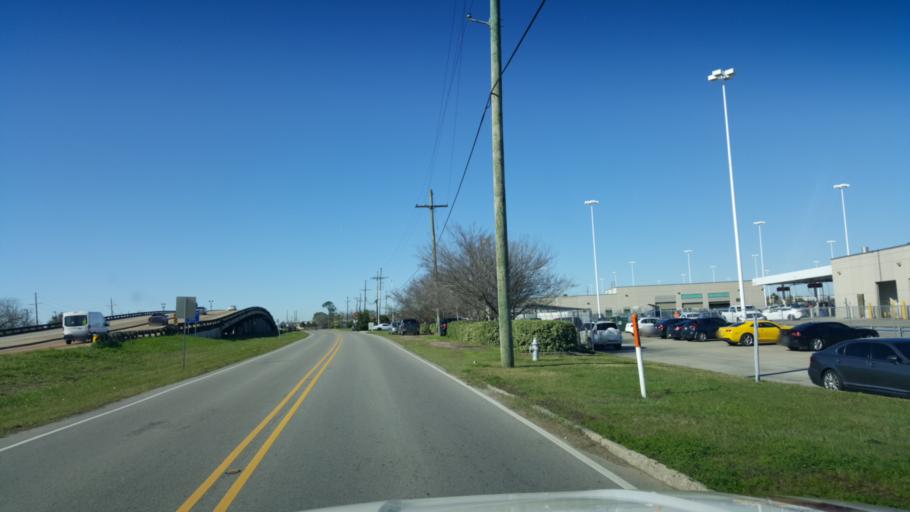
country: US
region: Louisiana
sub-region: Jefferson Parish
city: Kenner
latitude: 29.9837
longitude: -90.2639
